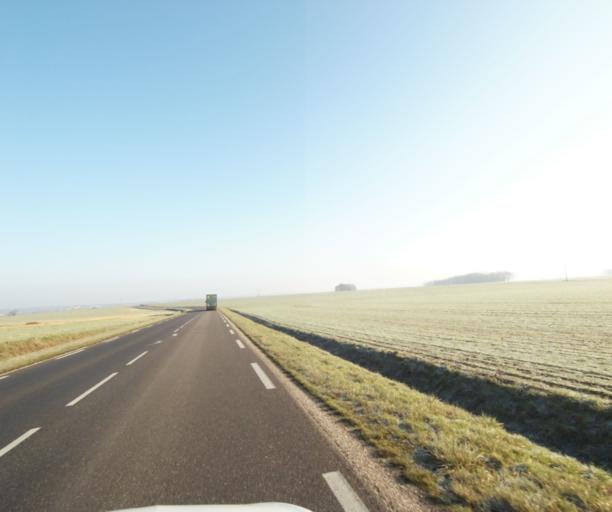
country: FR
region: Champagne-Ardenne
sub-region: Departement de la Haute-Marne
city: Montier-en-Der
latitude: 48.4552
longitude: 4.7459
